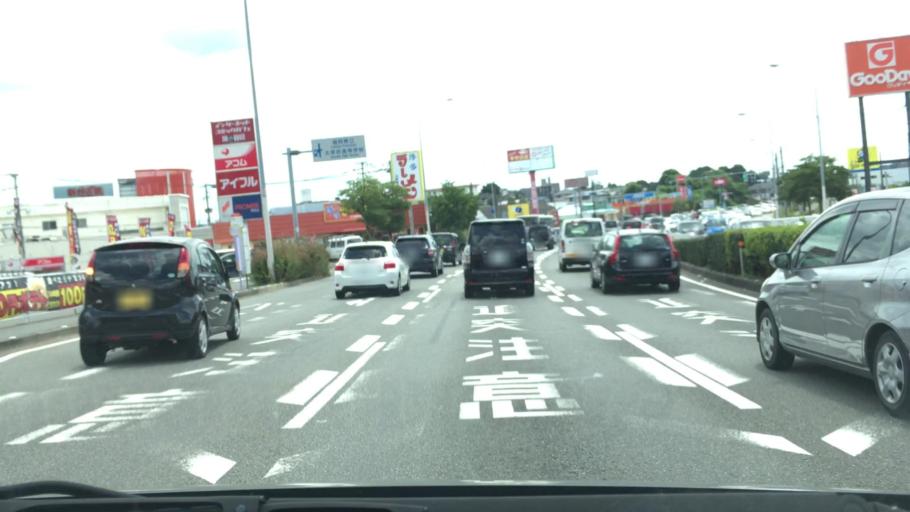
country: JP
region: Fukuoka
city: Chikushino-shi
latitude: 33.4955
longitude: 130.5351
